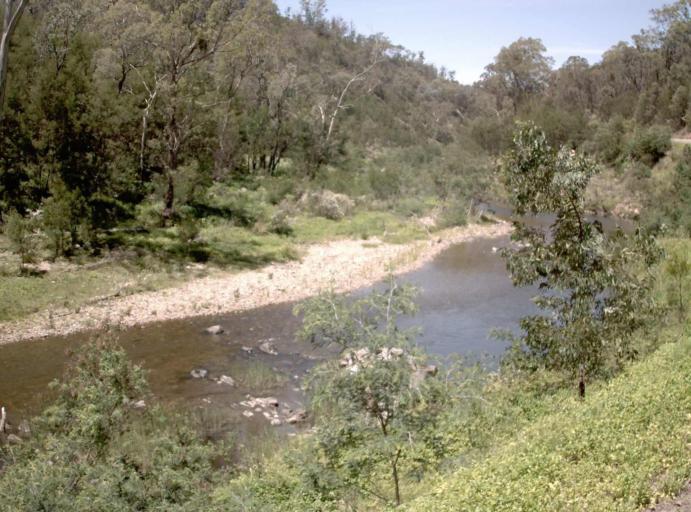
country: AU
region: Victoria
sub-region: East Gippsland
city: Bairnsdale
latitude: -37.4435
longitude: 147.8293
